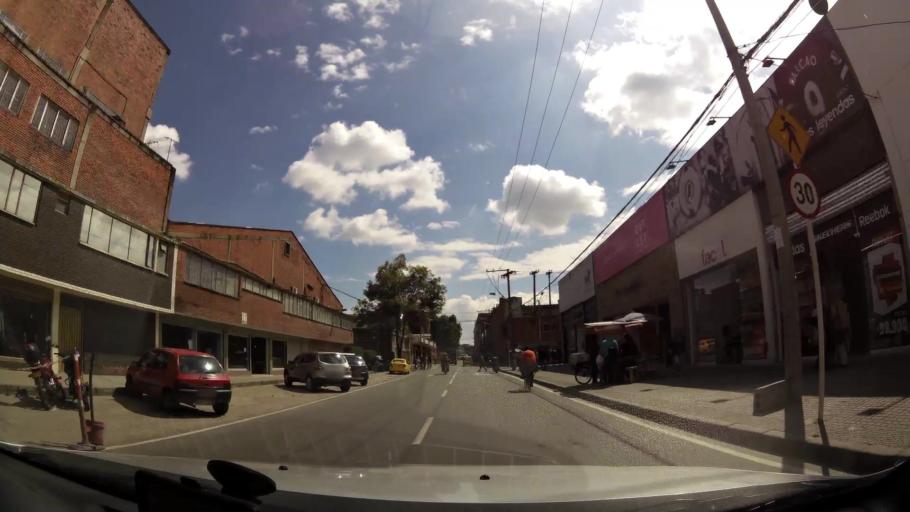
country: CO
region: Bogota D.C.
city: Bogota
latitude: 4.6312
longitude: -74.1130
